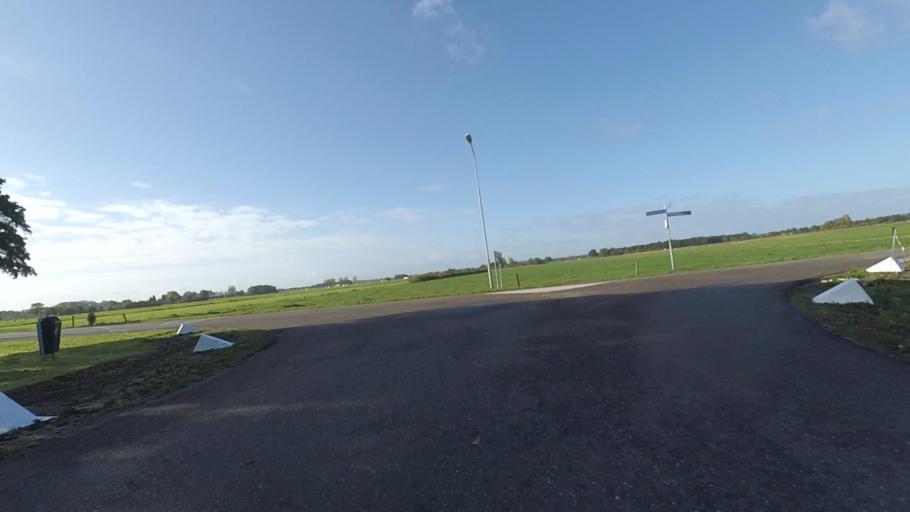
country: NL
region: Gelderland
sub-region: Gemeente Ermelo
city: Horst
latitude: 52.2945
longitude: 5.5653
